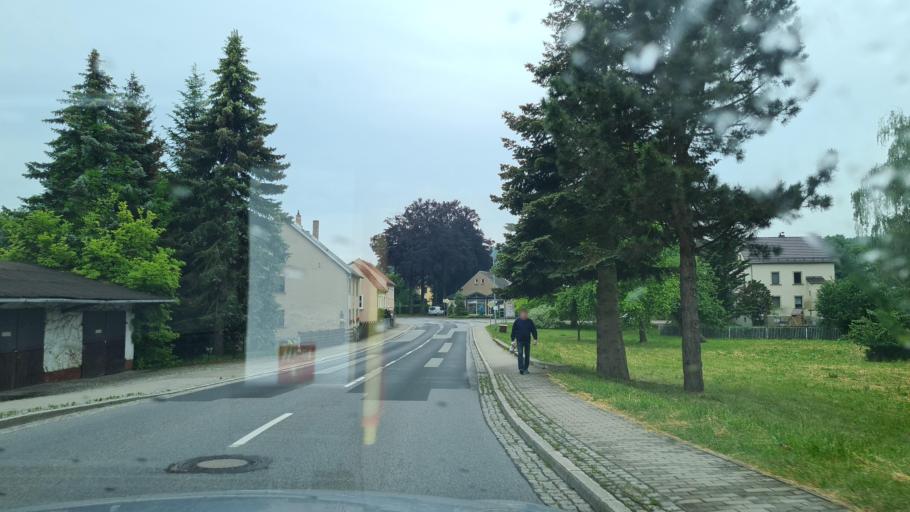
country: DE
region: Saxony
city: Grosspostwitz
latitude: 51.1178
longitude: 14.4404
